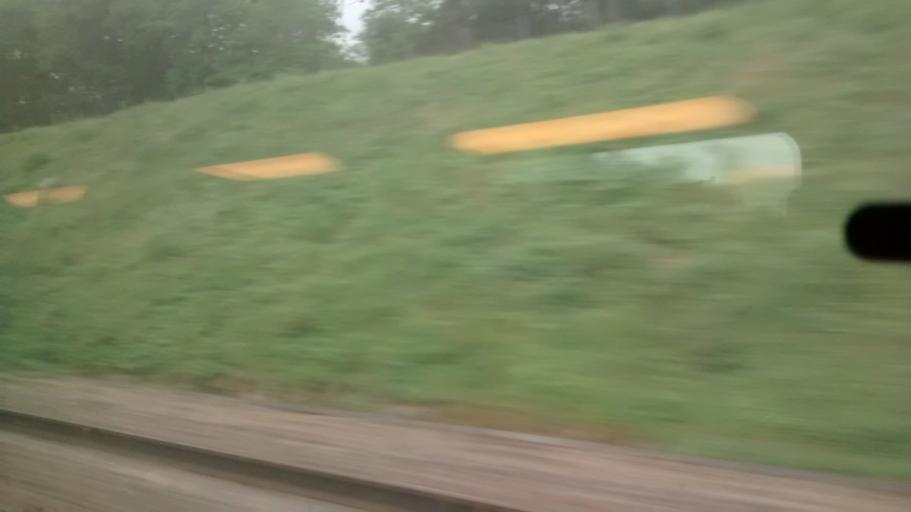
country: FR
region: Ile-de-France
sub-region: Departement de Seine-et-Marne
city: Montereau-Fault-Yonne
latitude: 48.4035
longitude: 2.9695
